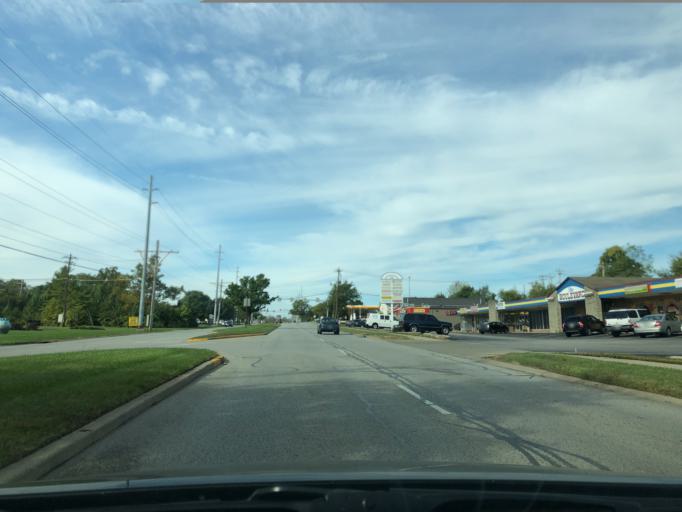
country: US
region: Ohio
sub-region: Hamilton County
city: Springdale
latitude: 39.2826
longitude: -84.4825
